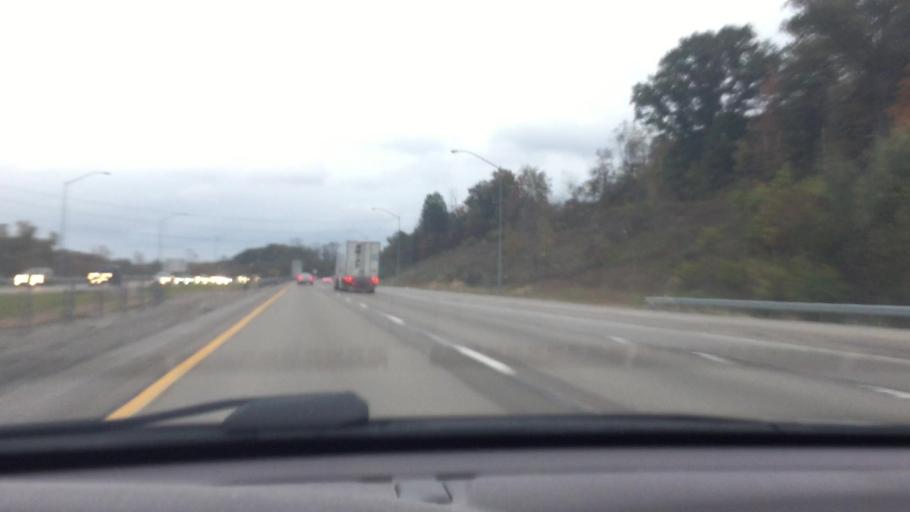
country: US
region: Pennsylvania
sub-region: Allegheny County
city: Carnegie
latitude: 40.4307
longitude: -80.1074
